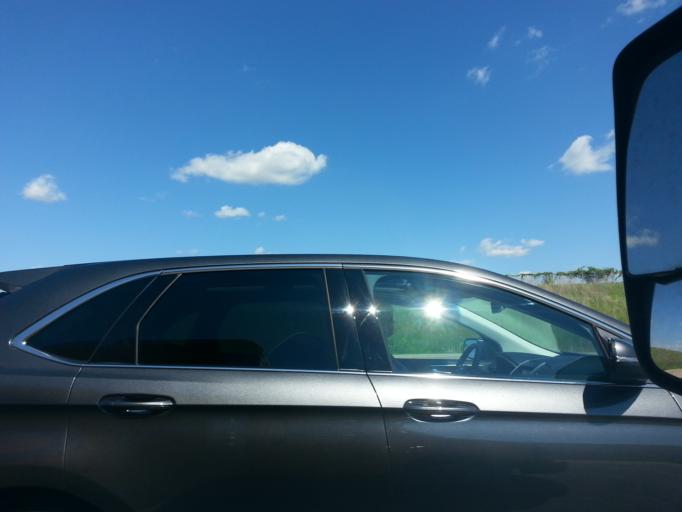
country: US
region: Illinois
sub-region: Winnebago County
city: Cherry Valley
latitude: 42.2880
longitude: -88.9649
